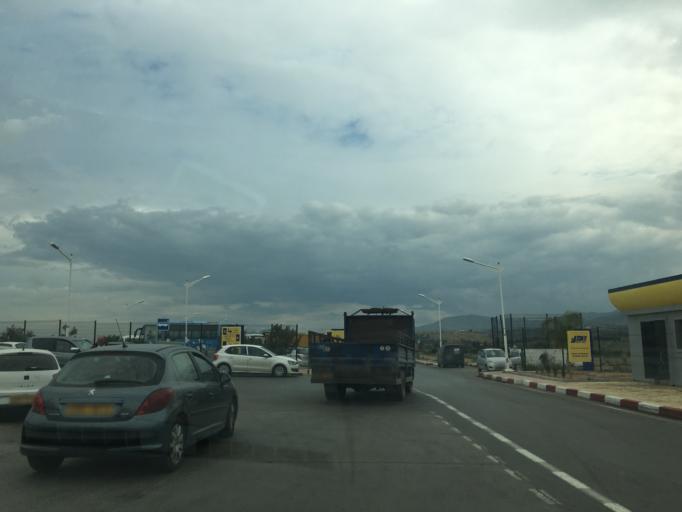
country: DZ
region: Bouira
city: Bouira
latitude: 36.3099
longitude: 4.0609
